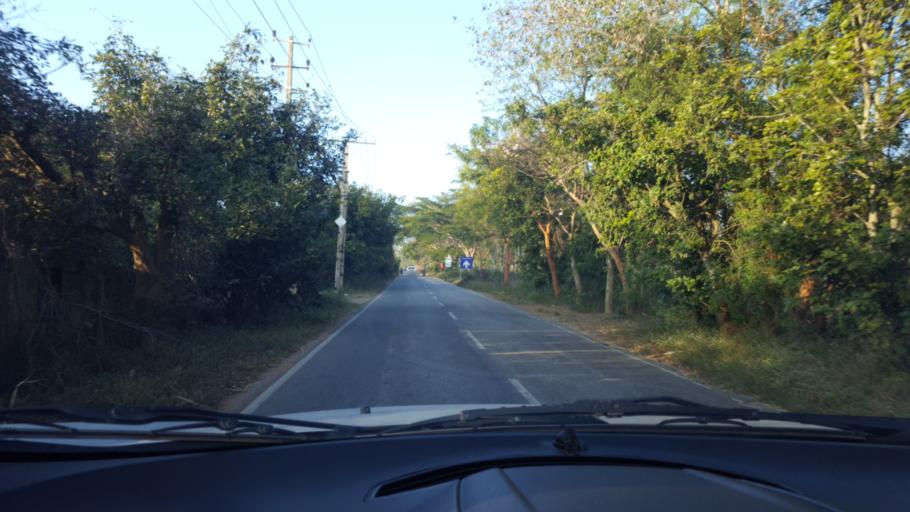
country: IN
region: Karnataka
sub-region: Bangalore Urban
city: Yelahanka
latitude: 13.1772
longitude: 77.5992
